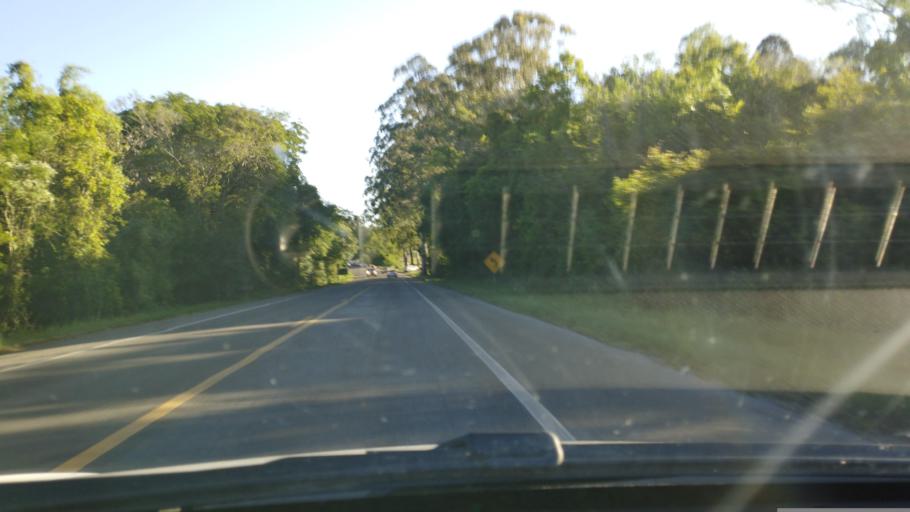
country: BR
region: Rio Grande do Sul
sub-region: Santa Maria
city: Santa Maria
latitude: -29.5959
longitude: -53.7670
